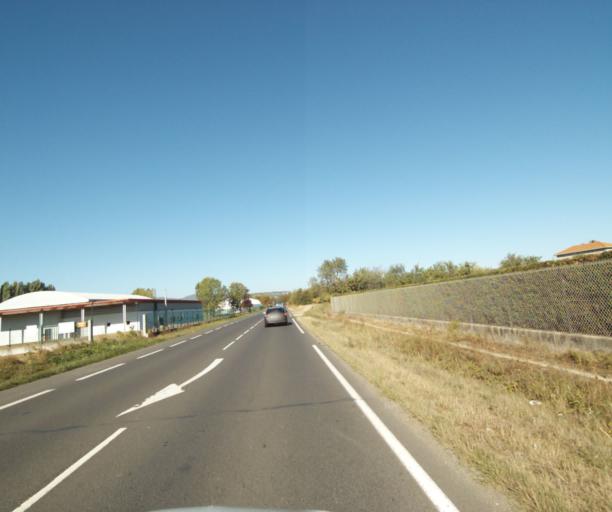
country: FR
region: Auvergne
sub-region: Departement du Puy-de-Dome
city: Gerzat
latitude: 45.8242
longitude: 3.1334
